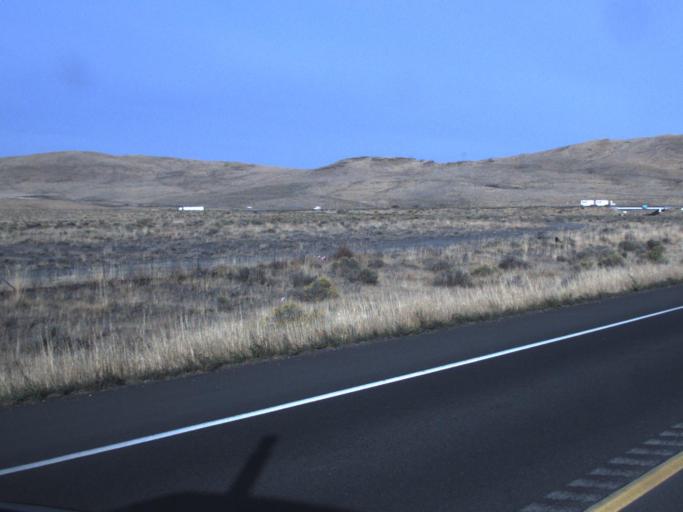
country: US
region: Oregon
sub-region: Umatilla County
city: Umatilla
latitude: 45.9440
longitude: -119.3440
